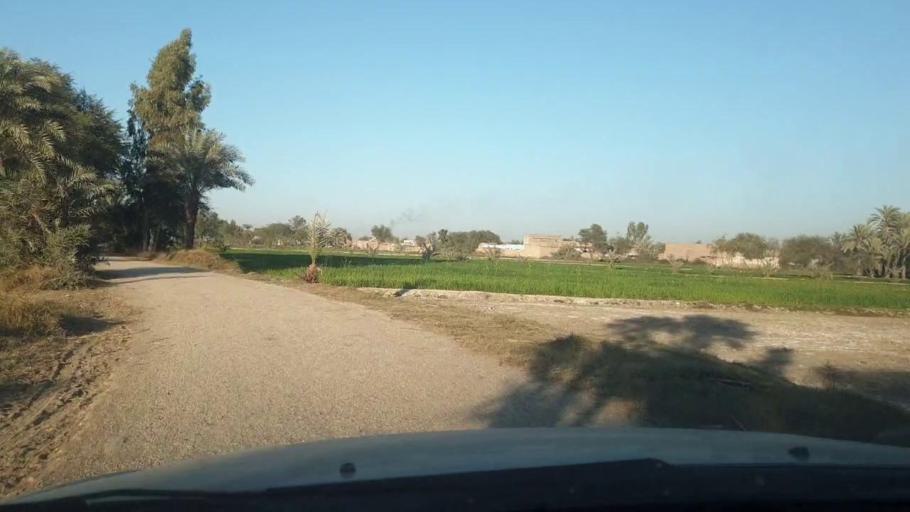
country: PK
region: Sindh
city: Ghotki
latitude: 28.0242
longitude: 69.3081
